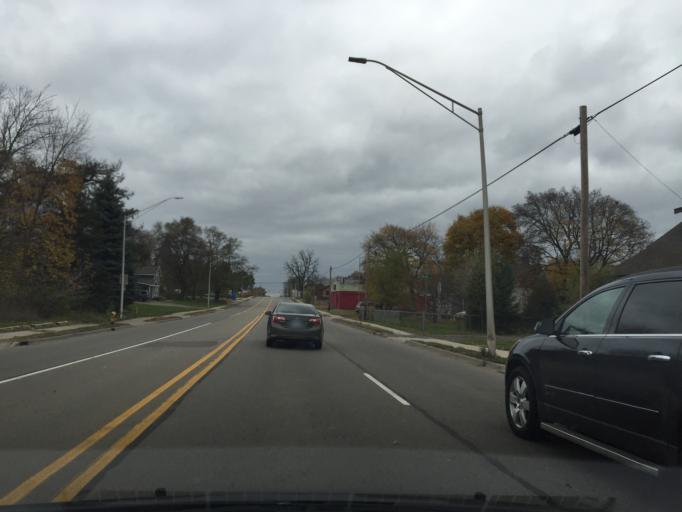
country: US
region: Michigan
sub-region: Oakland County
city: Pontiac
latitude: 42.6466
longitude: -83.3017
